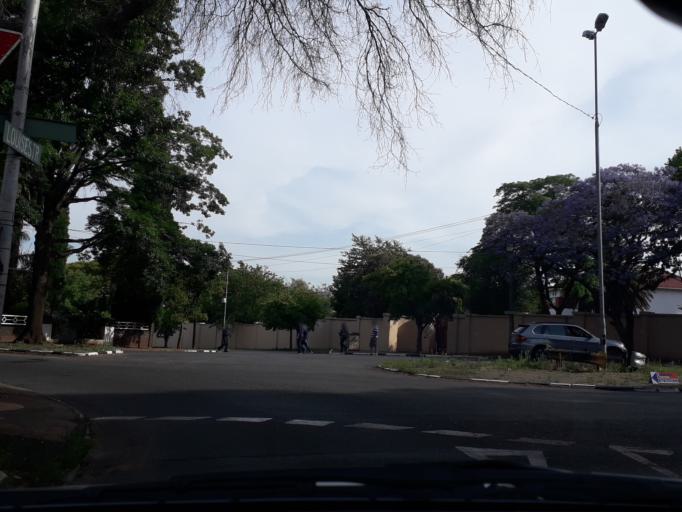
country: ZA
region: Gauteng
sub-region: City of Johannesburg Metropolitan Municipality
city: Johannesburg
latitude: -26.1709
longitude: 28.0900
